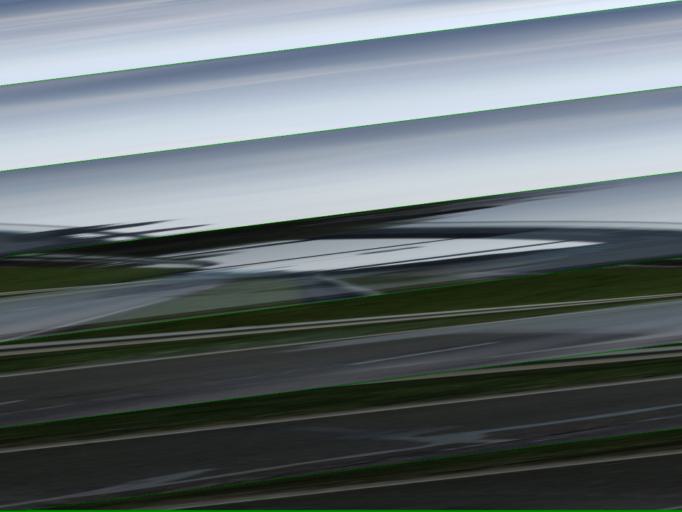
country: FR
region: Ile-de-France
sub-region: Departement des Yvelines
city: Houdan
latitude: 48.7727
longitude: 1.5529
